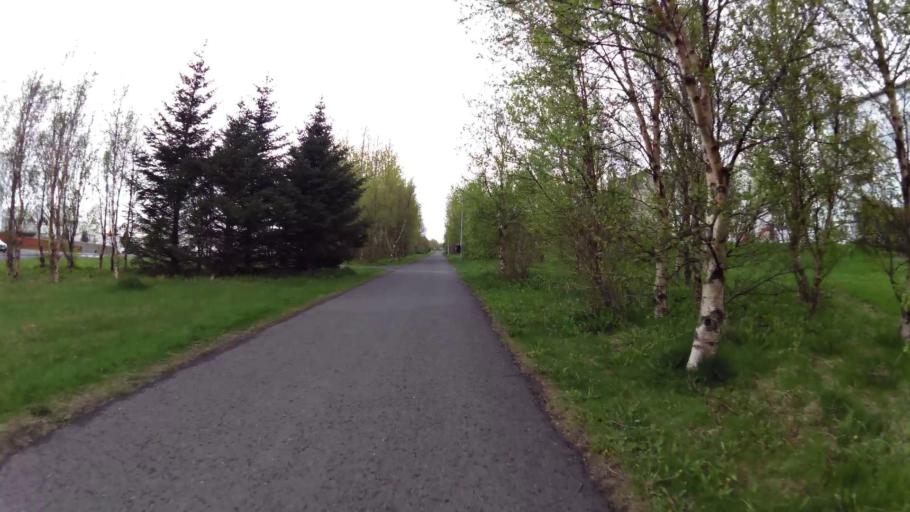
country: IS
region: Capital Region
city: Reykjavik
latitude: 64.1289
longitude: -21.8581
